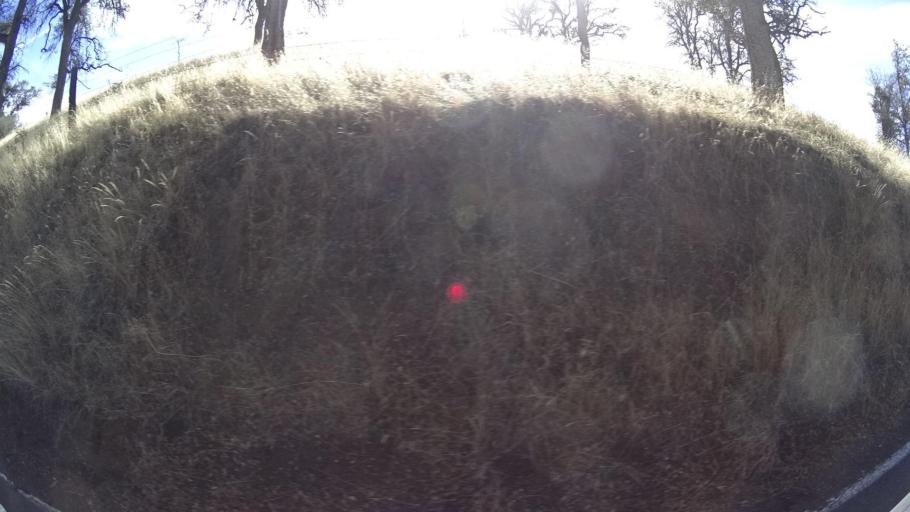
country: US
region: California
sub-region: Kern County
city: Alta Sierra
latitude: 35.6605
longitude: -118.7480
